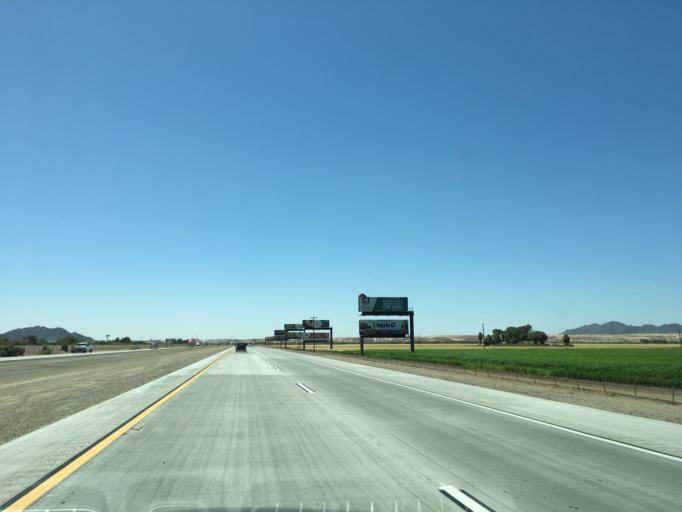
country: US
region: Arizona
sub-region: Yuma County
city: Yuma
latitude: 32.7386
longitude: -114.6673
